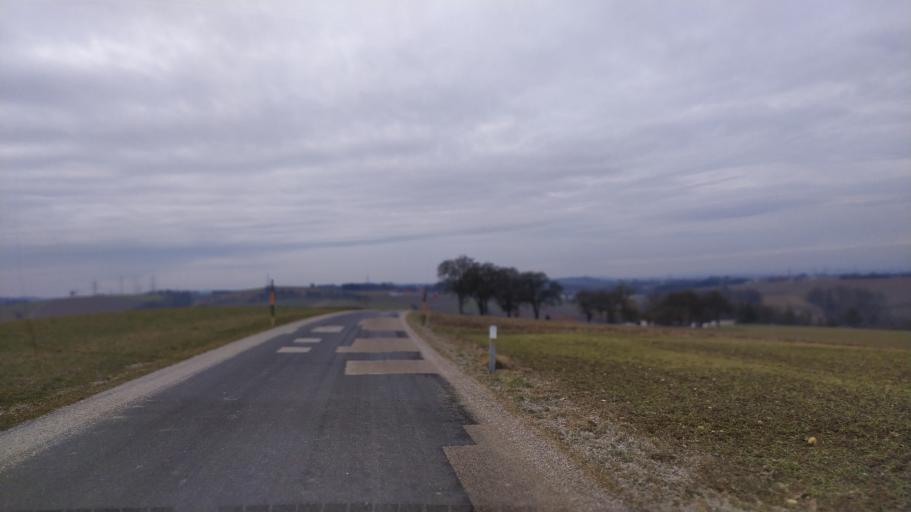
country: AT
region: Lower Austria
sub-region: Politischer Bezirk Amstetten
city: Zeillern
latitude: 48.1322
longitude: 14.7314
